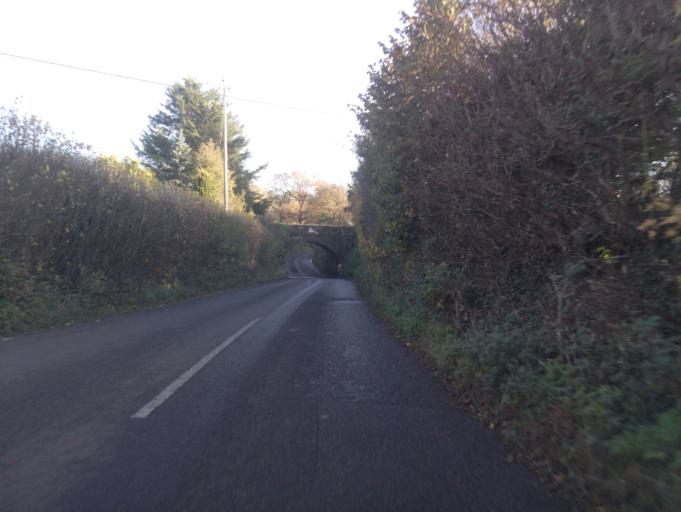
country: GB
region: England
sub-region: Somerset
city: Milborne Port
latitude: 50.9871
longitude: -2.4647
